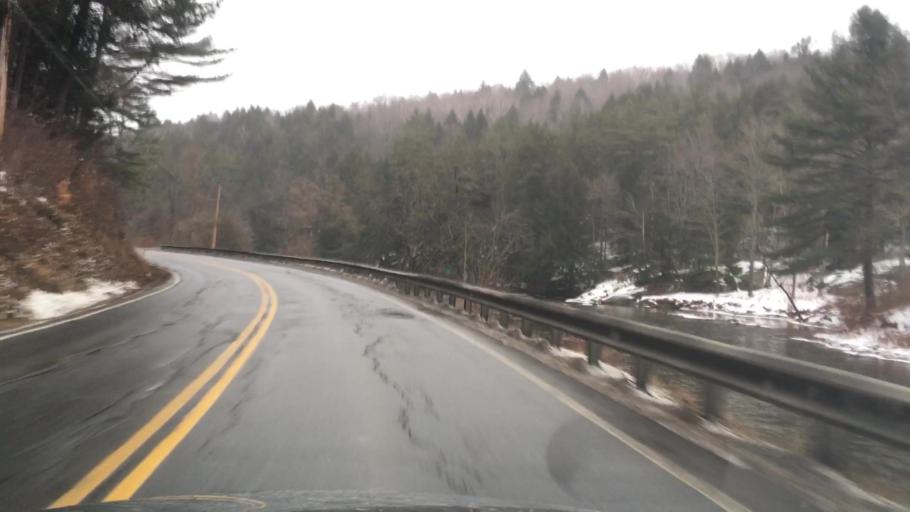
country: US
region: Vermont
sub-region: Windsor County
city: Chester
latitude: 43.3980
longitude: -72.5893
